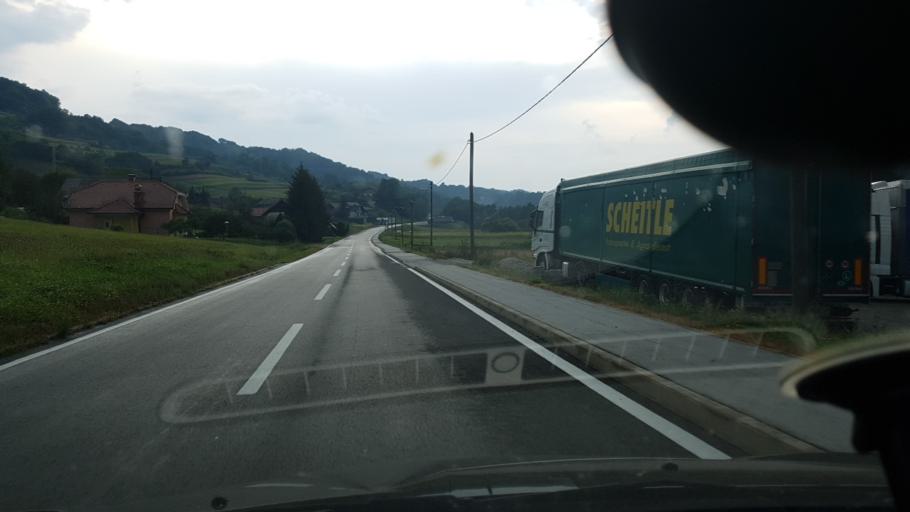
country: HR
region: Krapinsko-Zagorska
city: Pregrada
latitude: 46.2078
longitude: 15.7659
